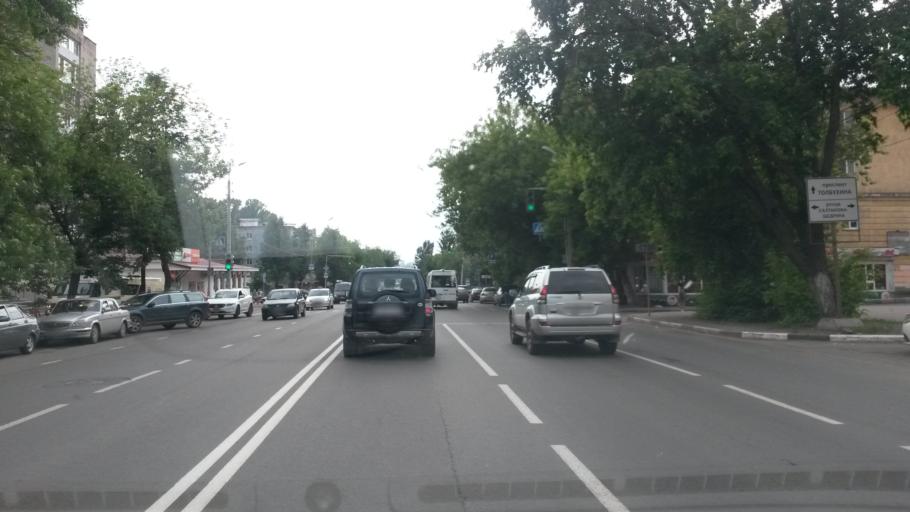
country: RU
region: Jaroslavl
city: Yaroslavl
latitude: 57.6246
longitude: 39.8579
